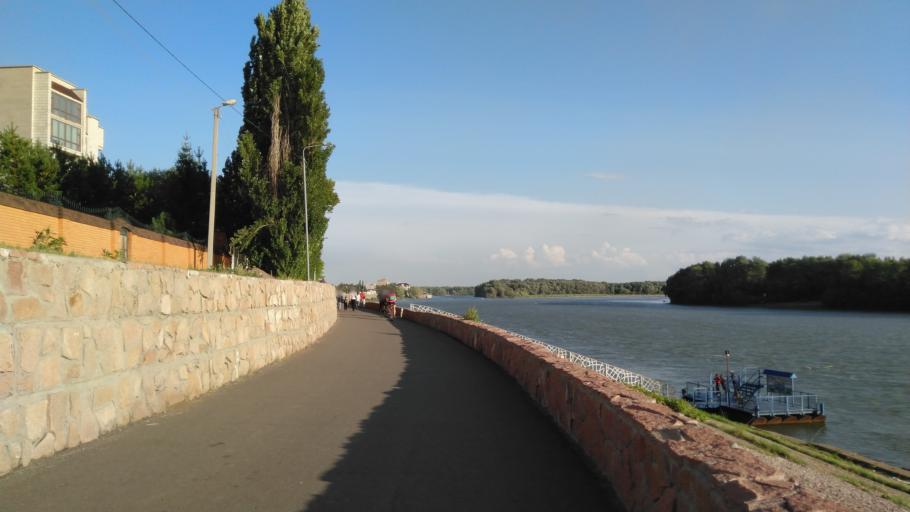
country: KZ
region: Pavlodar
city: Pavlodar
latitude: 52.2774
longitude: 76.9332
